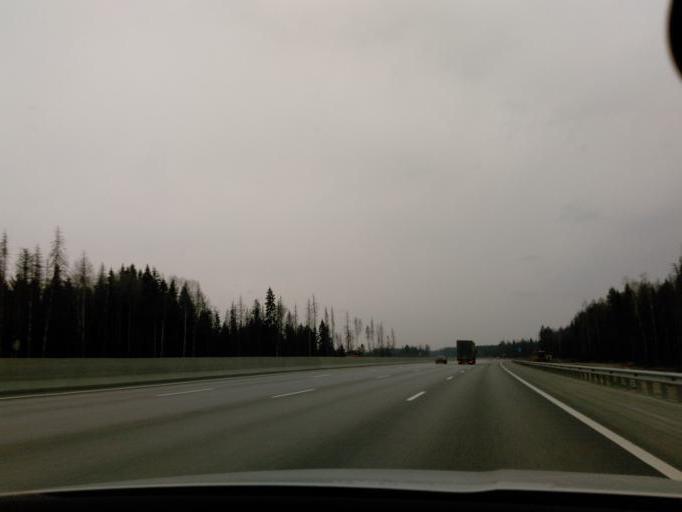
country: RU
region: Moskovskaya
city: Skhodnya
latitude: 55.9915
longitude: 37.3024
